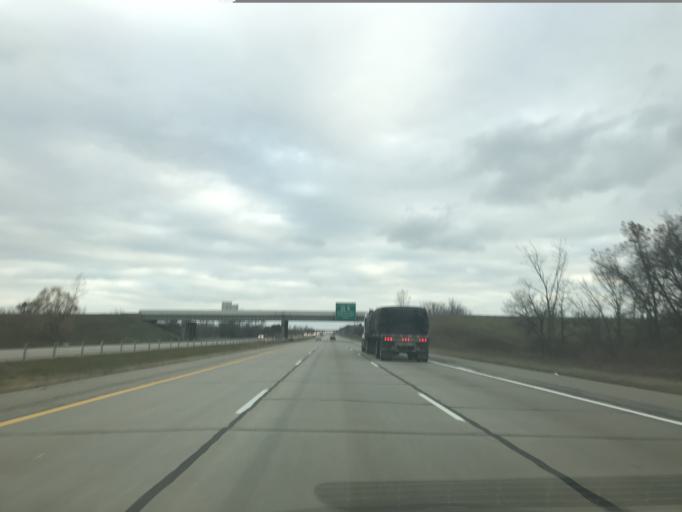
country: US
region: Michigan
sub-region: Eaton County
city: Waverly
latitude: 42.7182
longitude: -84.6689
